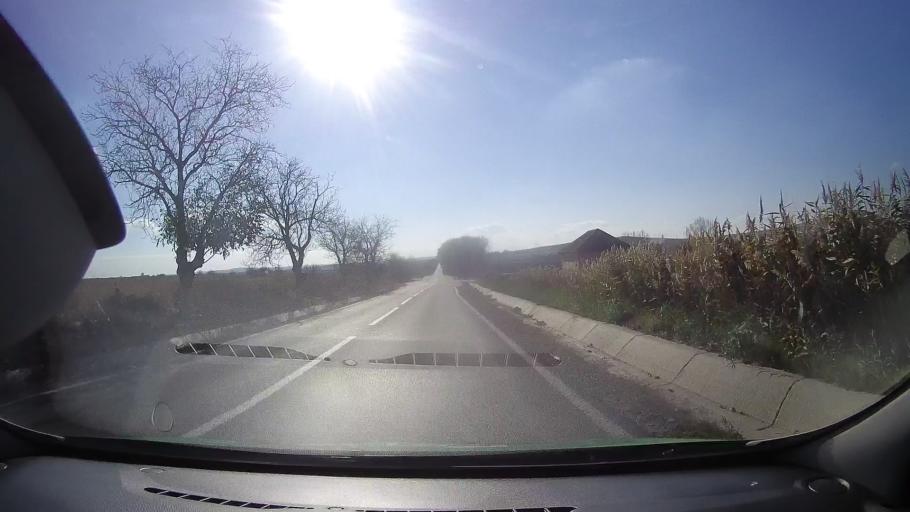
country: RO
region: Tulcea
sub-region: Comuna Ceamurlia de Jos
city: Ceamurlia de Jos
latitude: 44.7773
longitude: 28.6888
